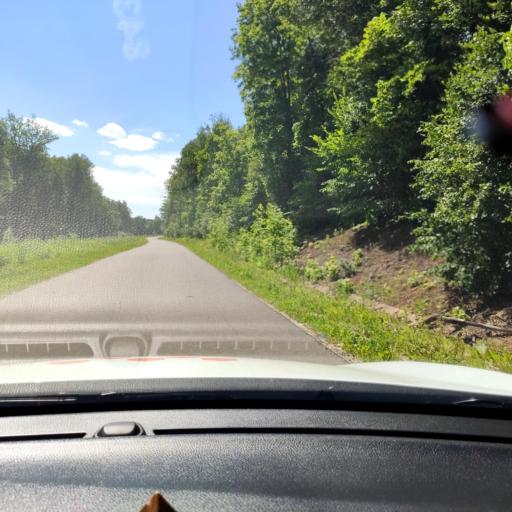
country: RU
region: Tatarstan
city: Sviyazhsk
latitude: 55.7741
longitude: 48.7762
